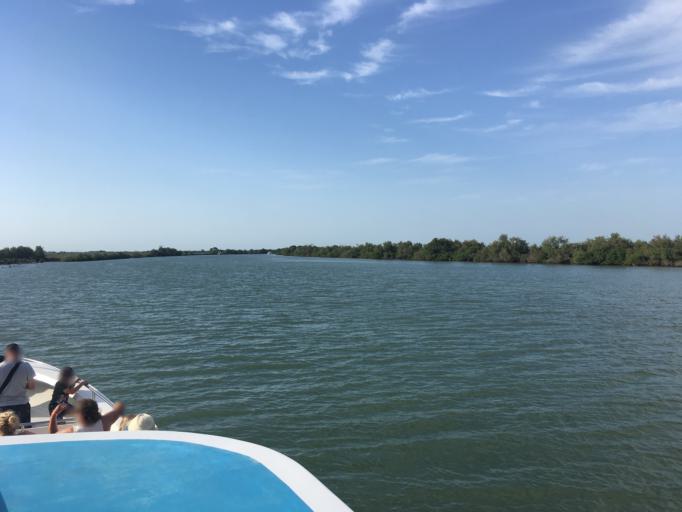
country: FR
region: Provence-Alpes-Cote d'Azur
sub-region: Departement des Bouches-du-Rhone
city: Saintes-Maries-de-la-Mer
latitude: 43.4707
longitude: 4.3784
